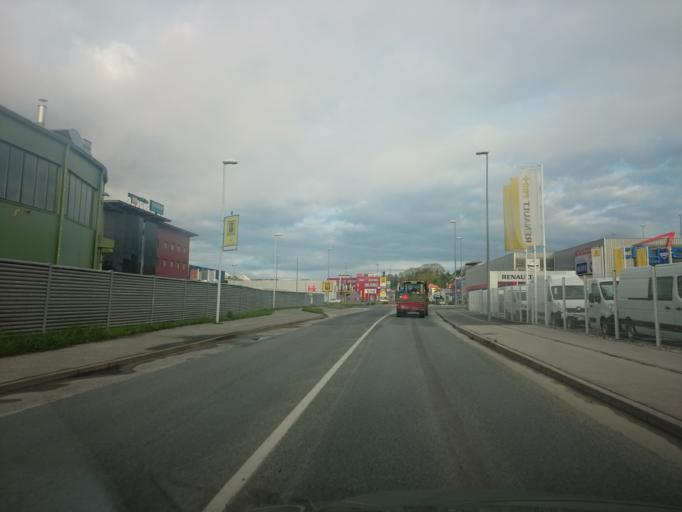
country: SI
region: Celje
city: Celje
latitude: 46.2398
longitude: 15.2808
